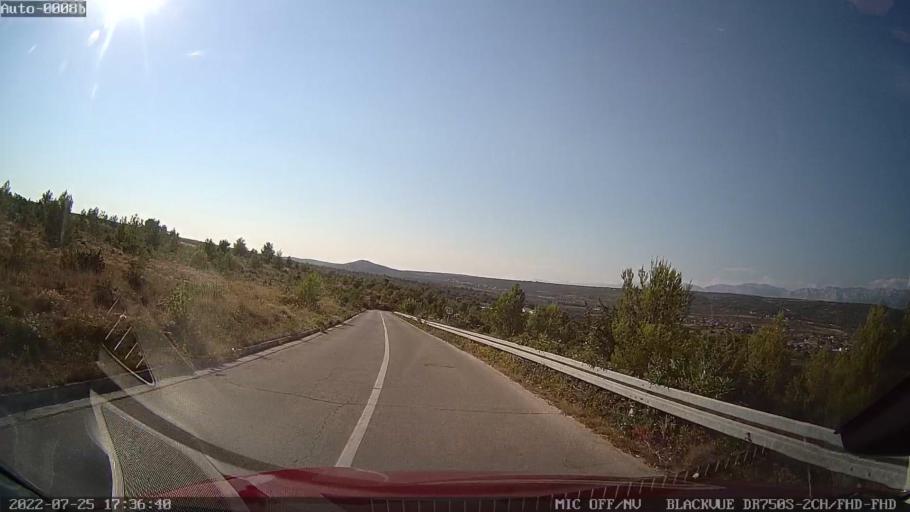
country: HR
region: Zadarska
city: Posedarje
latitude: 44.2026
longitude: 15.4701
